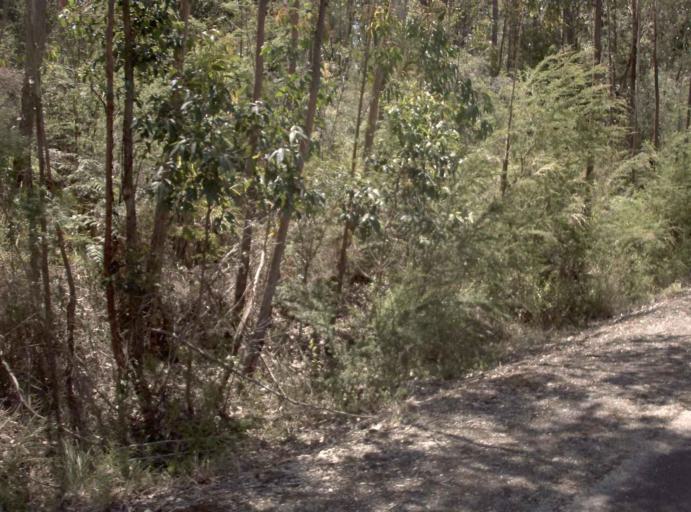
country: AU
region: Victoria
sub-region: East Gippsland
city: Lakes Entrance
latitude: -37.6951
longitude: 148.6126
